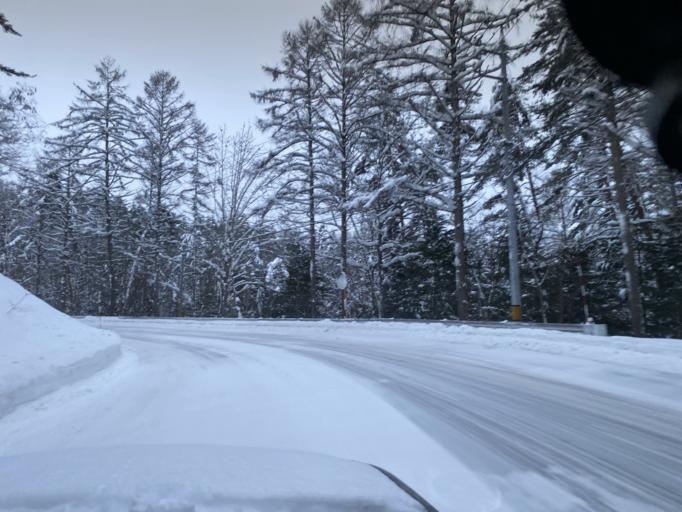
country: JP
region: Nagano
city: Omachi
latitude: 36.5632
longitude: 137.8675
